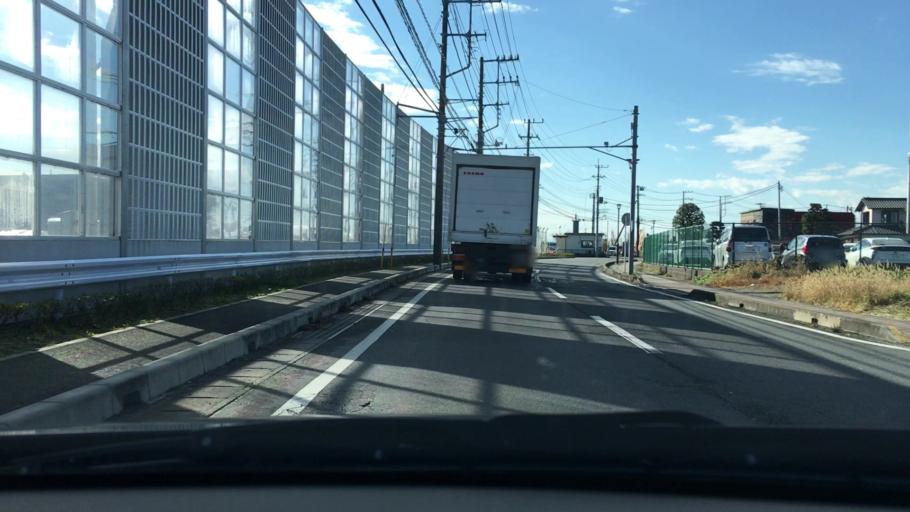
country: JP
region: Chiba
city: Narita
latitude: 35.7802
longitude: 140.3833
